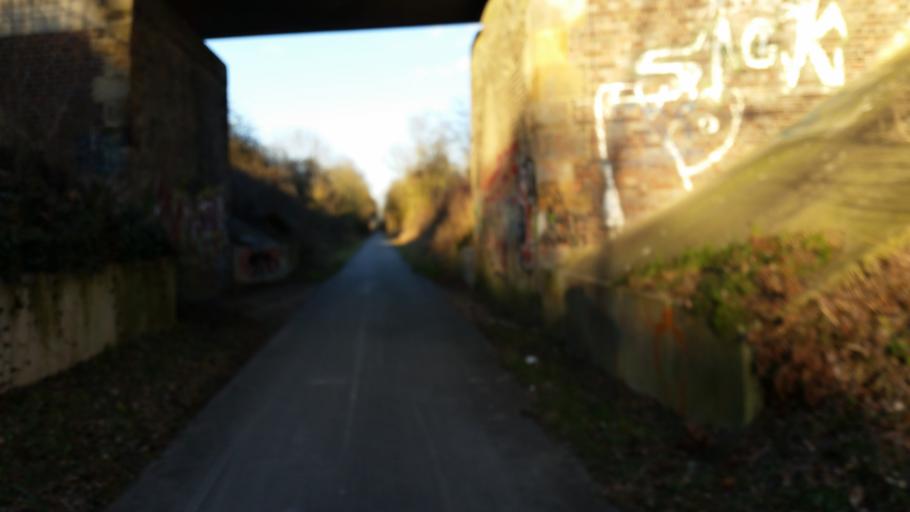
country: DE
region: North Rhine-Westphalia
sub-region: Regierungsbezirk Munster
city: Neuenkirchen
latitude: 52.2521
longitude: 7.3781
